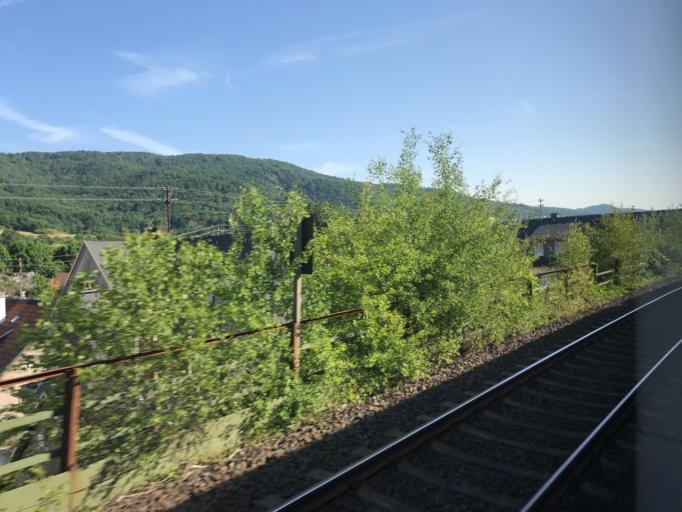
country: DE
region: Rheinland-Pfalz
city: Hintertiefenbach
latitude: 49.7141
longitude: 7.3694
